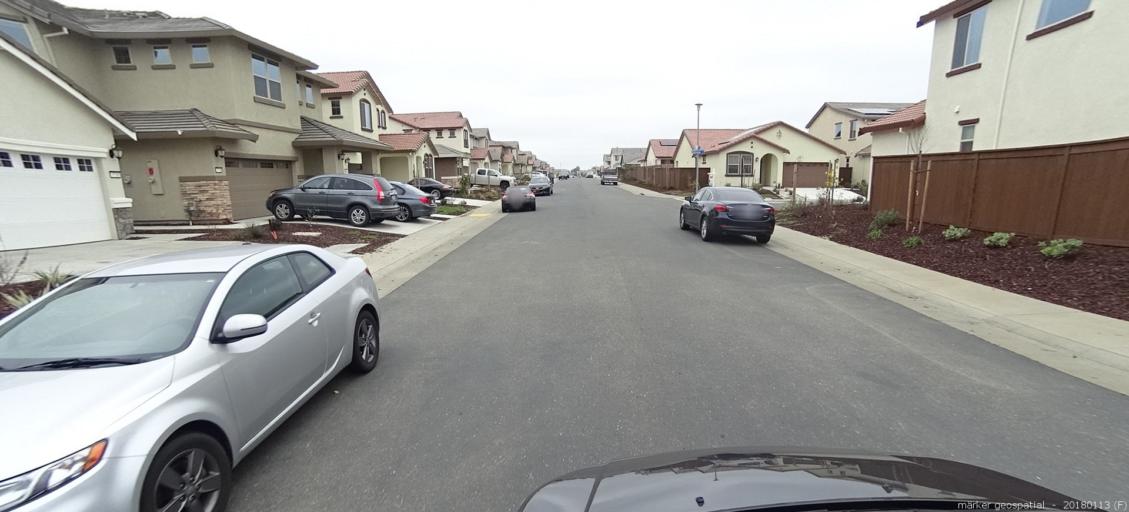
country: US
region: California
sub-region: Sacramento County
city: Gold River
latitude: 38.5656
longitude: -121.2019
